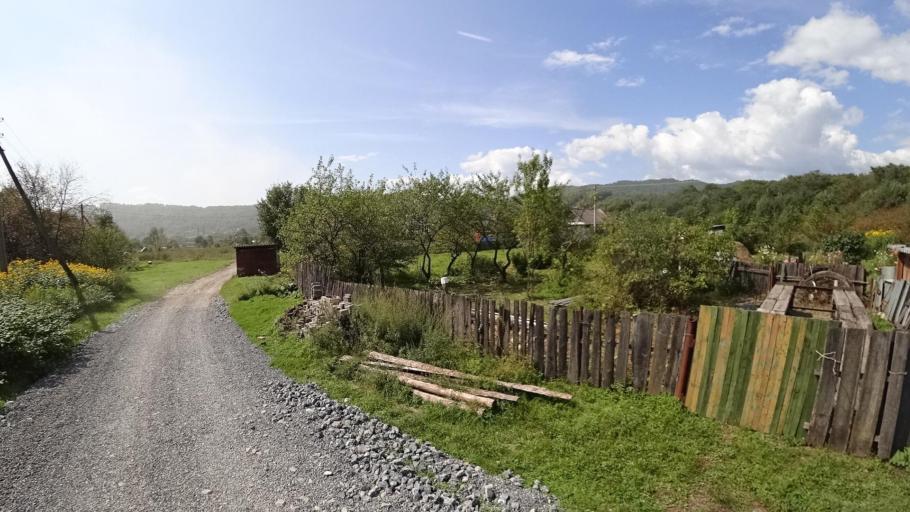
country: RU
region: Jewish Autonomous Oblast
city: Londoko
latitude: 49.0279
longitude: 131.9345
